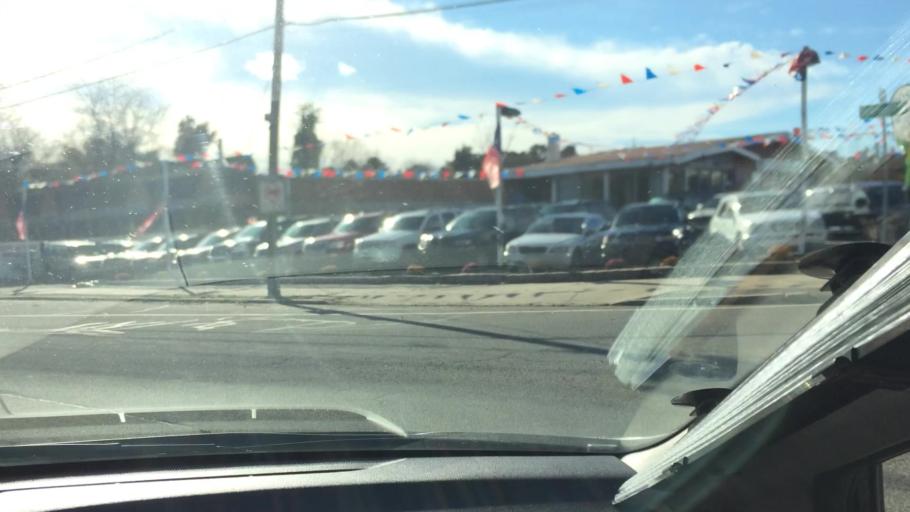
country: US
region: New York
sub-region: Suffolk County
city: Wyandanch
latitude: 40.7417
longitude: -73.3462
